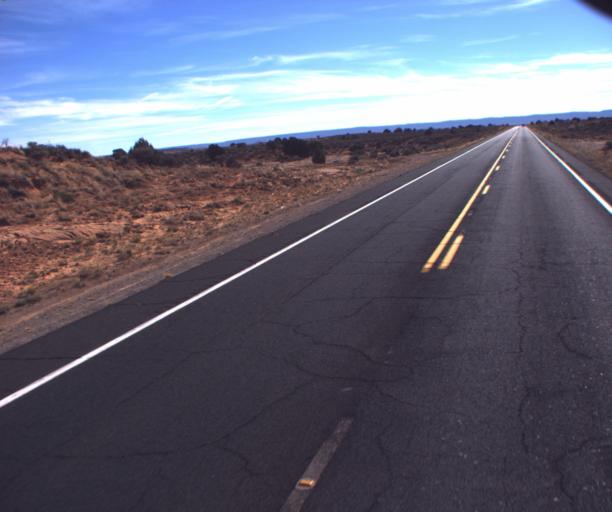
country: US
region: Arizona
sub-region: Coconino County
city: Kaibito
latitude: 36.5714
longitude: -110.7656
